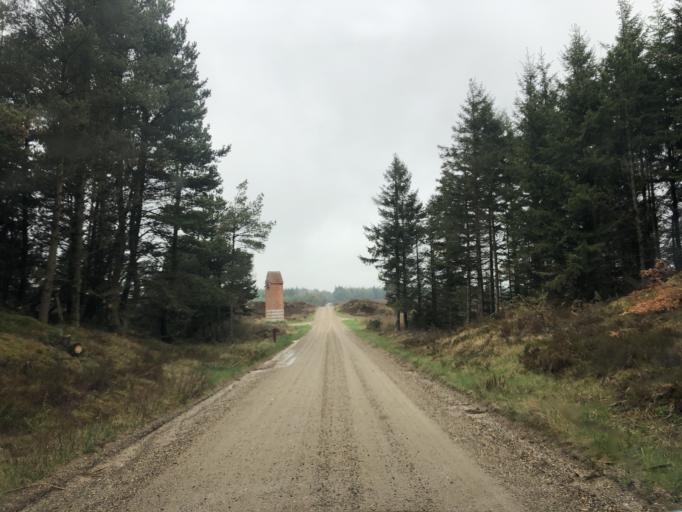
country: DK
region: Central Jutland
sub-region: Lemvig Kommune
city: Lemvig
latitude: 56.4715
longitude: 8.3837
